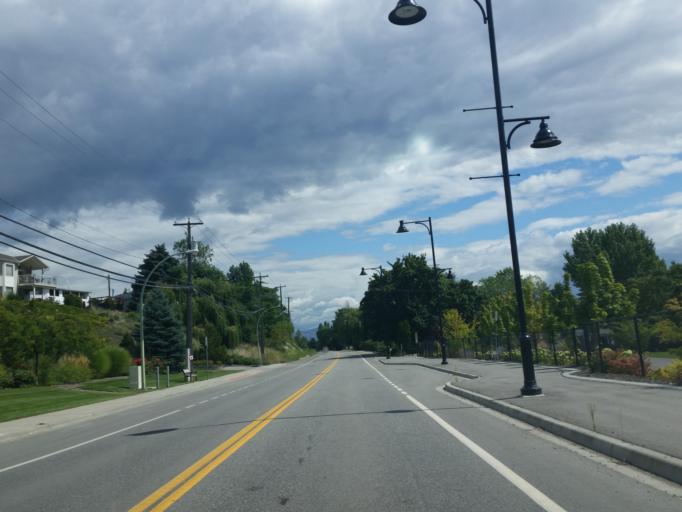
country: CA
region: British Columbia
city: West Kelowna
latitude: 49.8251
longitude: -119.6101
